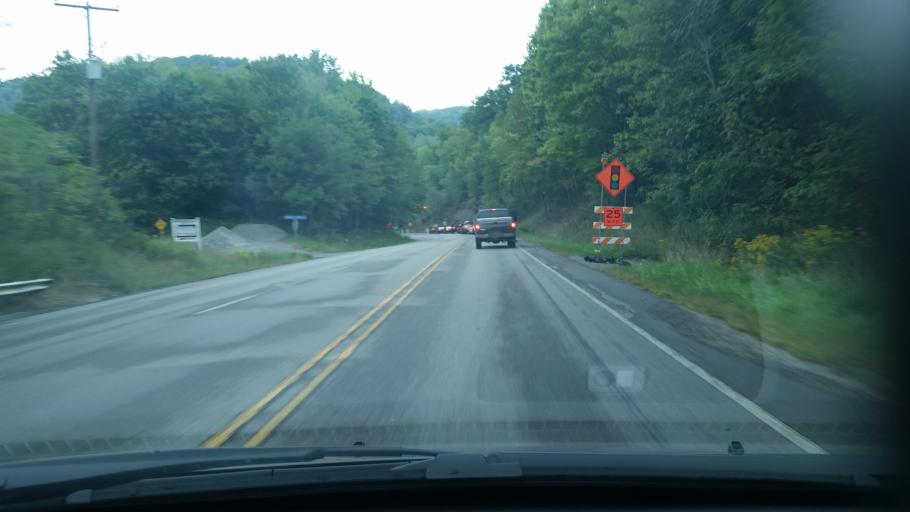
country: US
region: Pennsylvania
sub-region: Clearfield County
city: Shiloh
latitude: 41.0681
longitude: -78.3564
